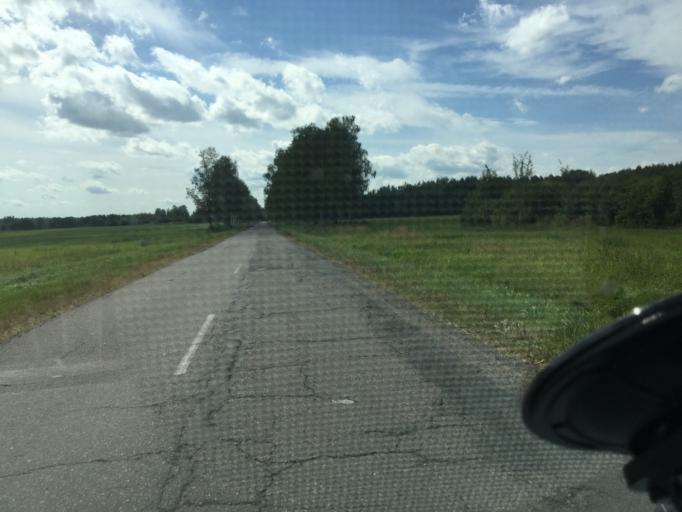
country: BY
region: Vitebsk
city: Chashniki
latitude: 55.3080
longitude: 29.4028
